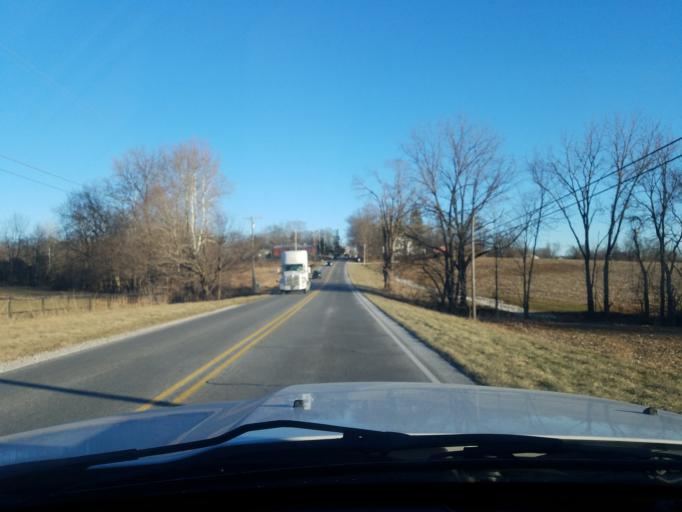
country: US
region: Indiana
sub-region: Floyd County
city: Galena
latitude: 38.3760
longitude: -85.9973
